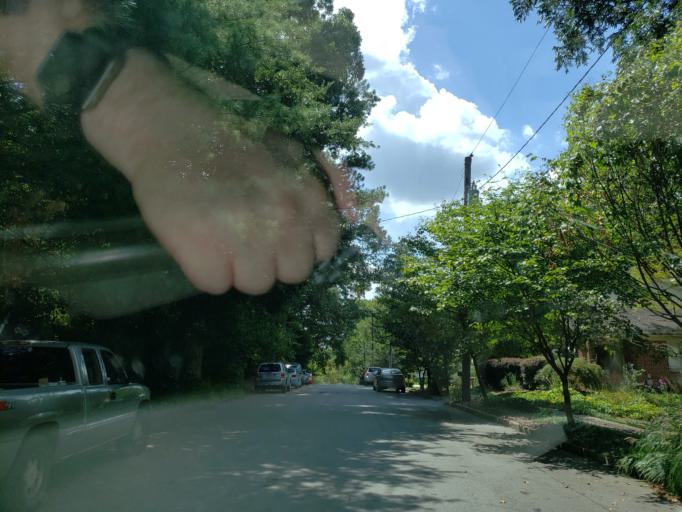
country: US
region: Georgia
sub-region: DeKalb County
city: Druid Hills
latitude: 33.7926
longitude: -84.3594
